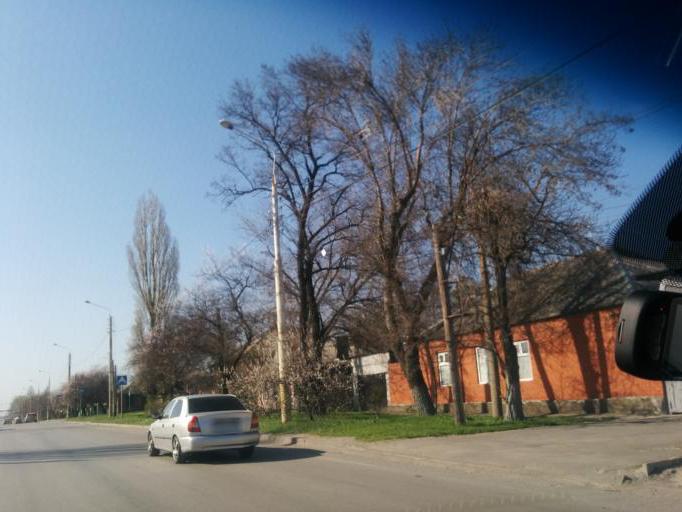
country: RU
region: Rostov
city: Shakhty
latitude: 47.7002
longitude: 40.2038
